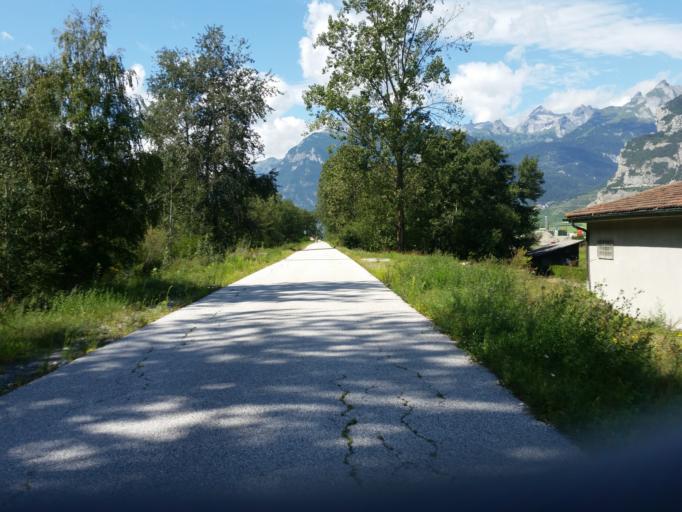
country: CH
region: Valais
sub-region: Conthey District
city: Basse-Nendaz
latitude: 46.2015
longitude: 7.2928
